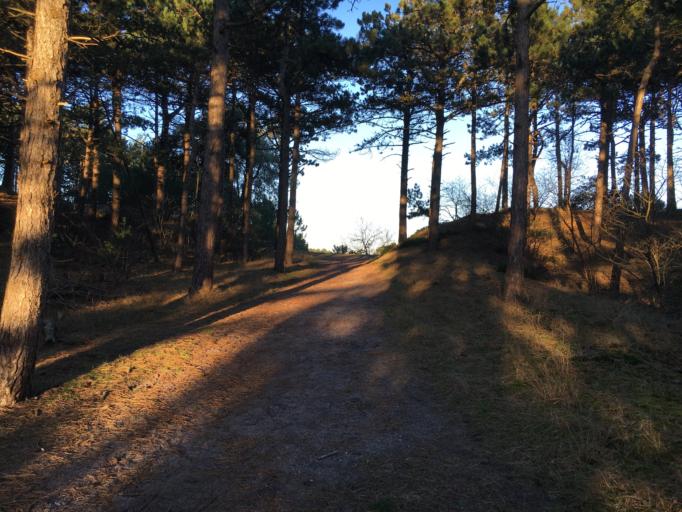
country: NL
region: North Holland
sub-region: Gemeente Bergen
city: Egmond aan Zee
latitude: 52.7144
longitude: 4.6736
